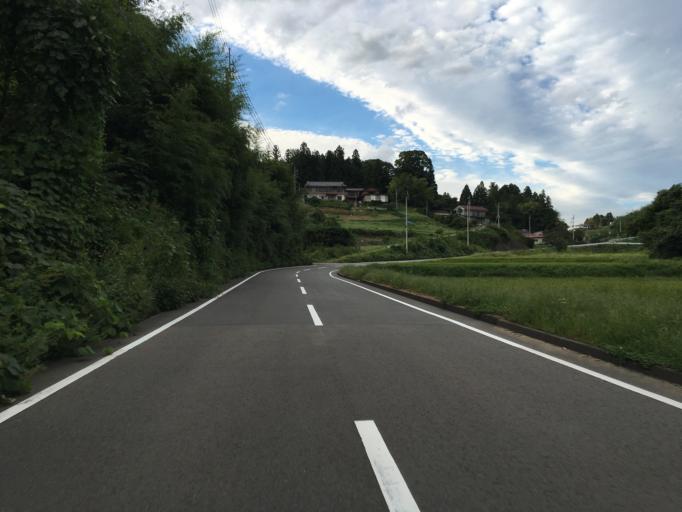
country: JP
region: Fukushima
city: Nihommatsu
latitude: 37.6035
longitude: 140.4968
